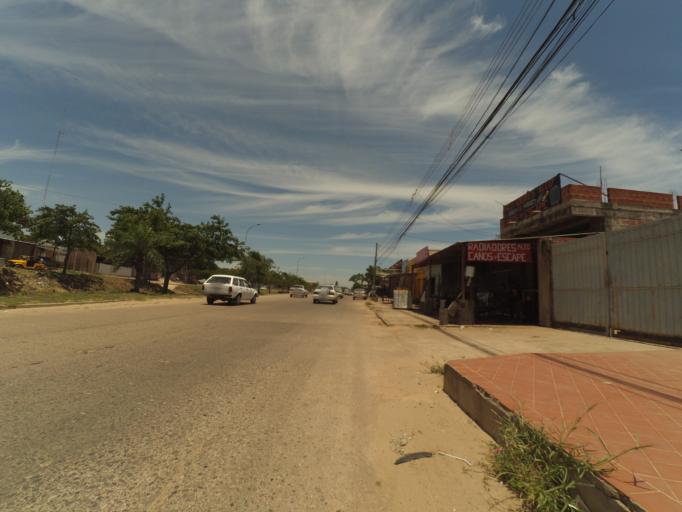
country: BO
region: Santa Cruz
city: Santa Cruz de la Sierra
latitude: -17.8106
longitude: -63.2180
